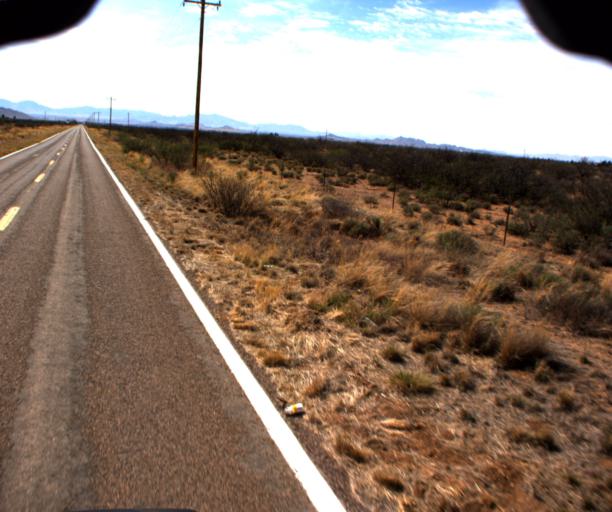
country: US
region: Arizona
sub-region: Cochise County
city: Willcox
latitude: 31.8761
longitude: -109.5541
